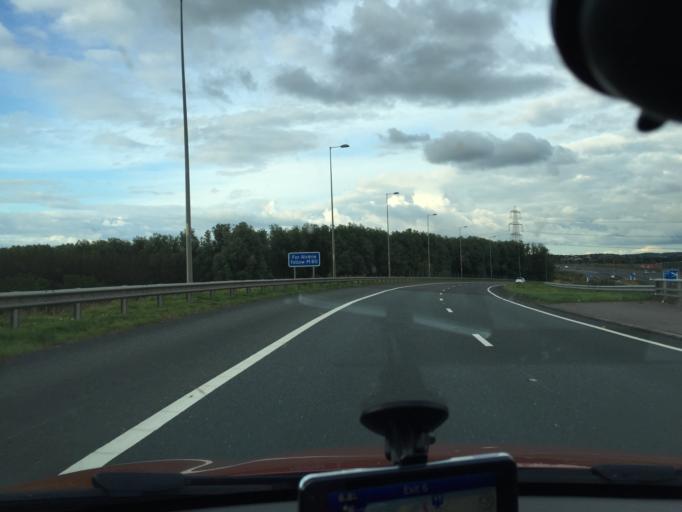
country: GB
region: Scotland
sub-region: North Lanarkshire
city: Glenboig
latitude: 55.9226
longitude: -4.0557
